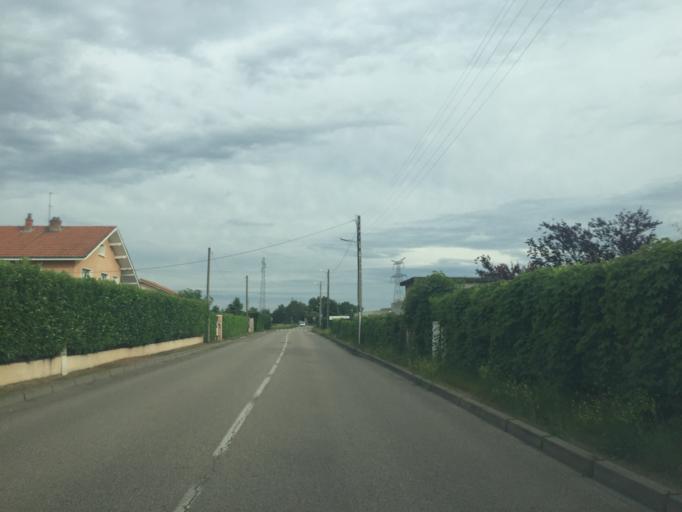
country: FR
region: Rhone-Alpes
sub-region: Departement de l'Ain
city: Beynost
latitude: 45.8322
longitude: 5.0087
